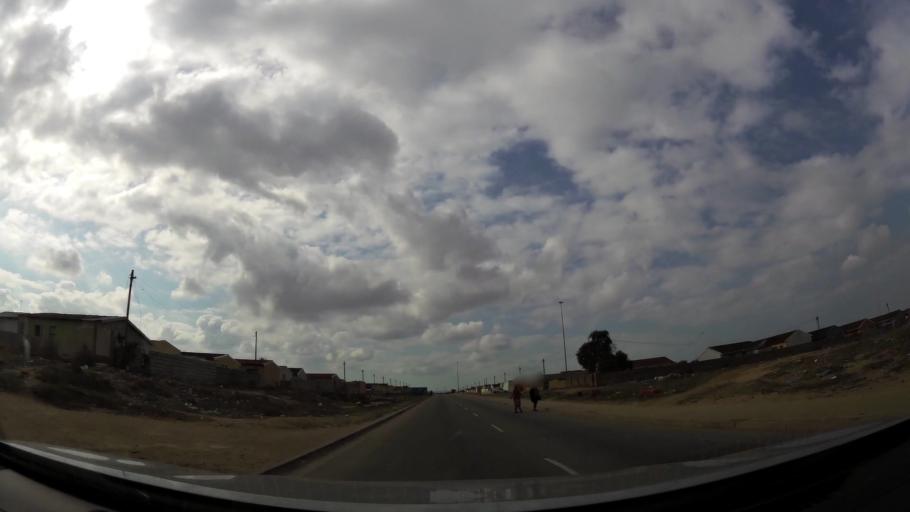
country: ZA
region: Eastern Cape
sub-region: Nelson Mandela Bay Metropolitan Municipality
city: Port Elizabeth
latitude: -33.8213
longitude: 25.5916
